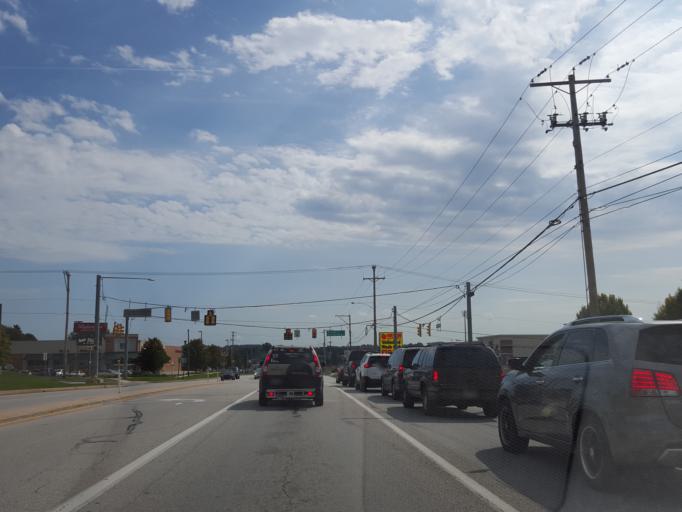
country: US
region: Pennsylvania
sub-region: York County
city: Valley View
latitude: 39.9365
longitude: -76.6926
